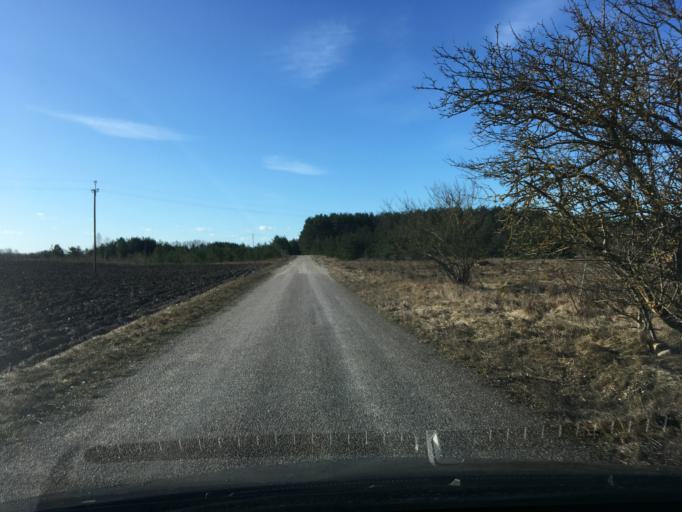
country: EE
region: Laeaene
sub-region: Lihula vald
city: Lihula
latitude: 58.5824
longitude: 23.7048
